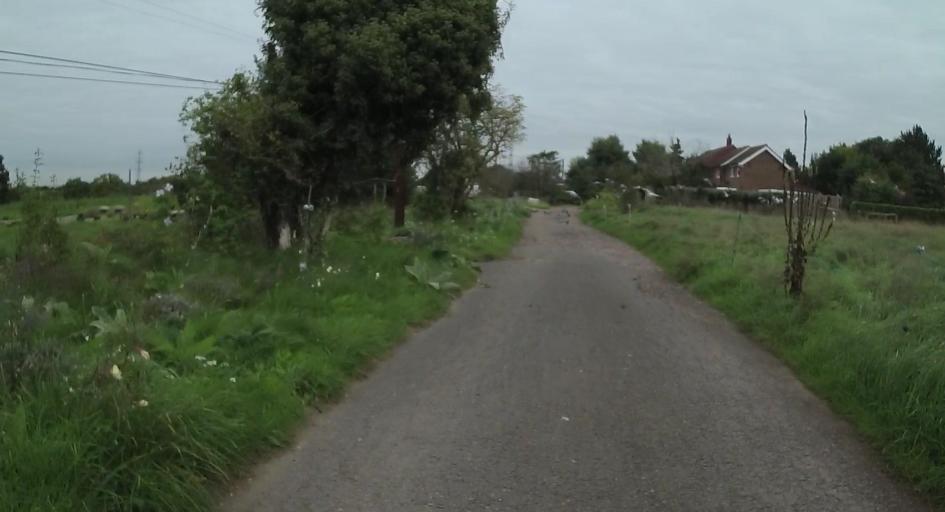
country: GB
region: England
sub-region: Surrey
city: Byfleet
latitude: 51.3263
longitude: -0.4832
